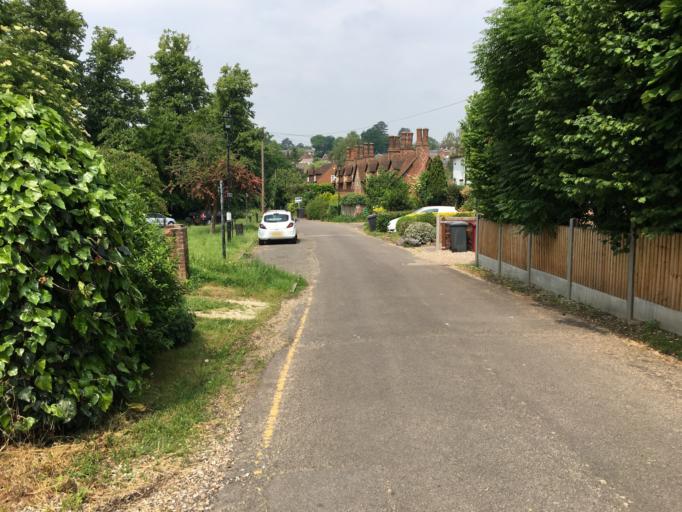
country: GB
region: England
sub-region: West Berkshire
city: Tilehurst
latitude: 51.4447
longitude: -1.0254
